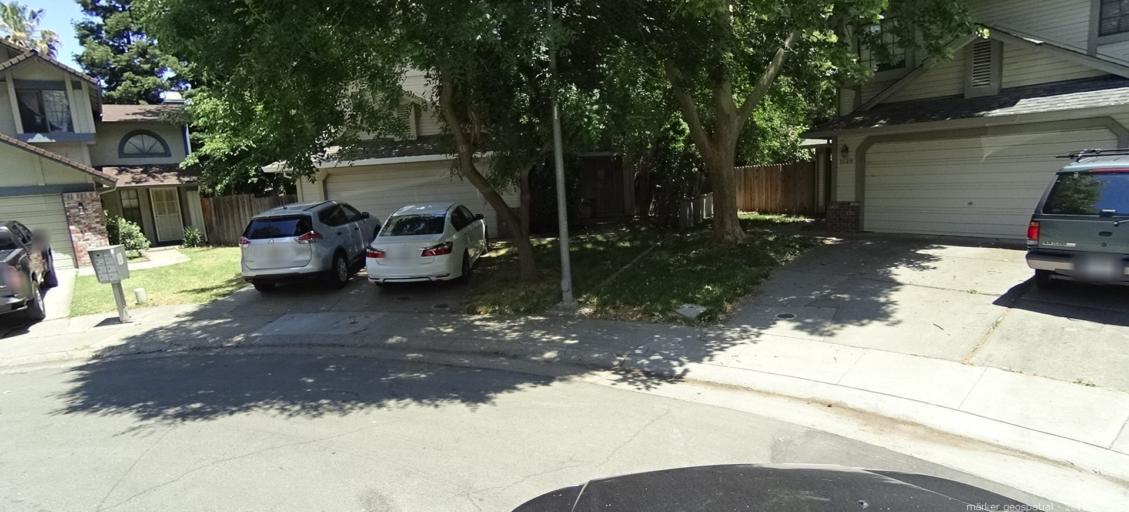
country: US
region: California
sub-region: Sacramento County
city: Sacramento
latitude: 38.6151
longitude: -121.4960
